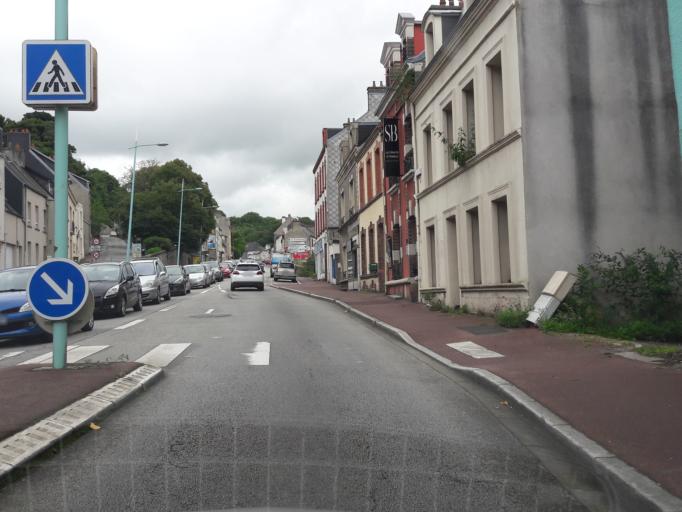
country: FR
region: Lower Normandy
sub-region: Departement de la Manche
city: Cherbourg-Octeville
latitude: 49.6267
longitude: -1.6175
